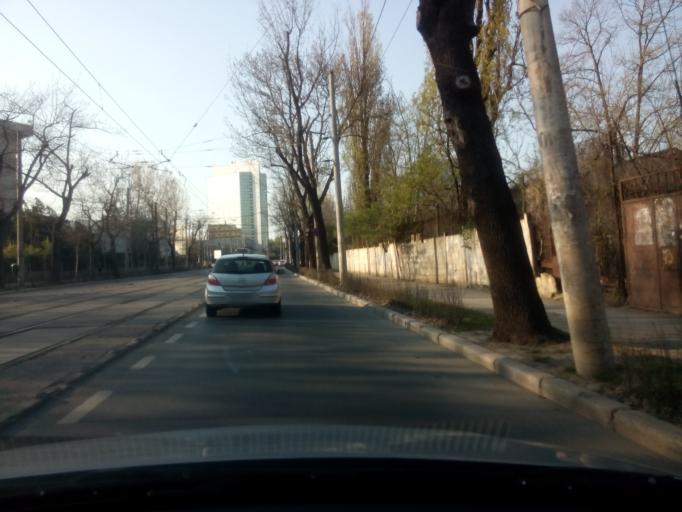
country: RO
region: Bucuresti
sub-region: Municipiul Bucuresti
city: Bucuresti
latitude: 44.4734
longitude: 26.0716
